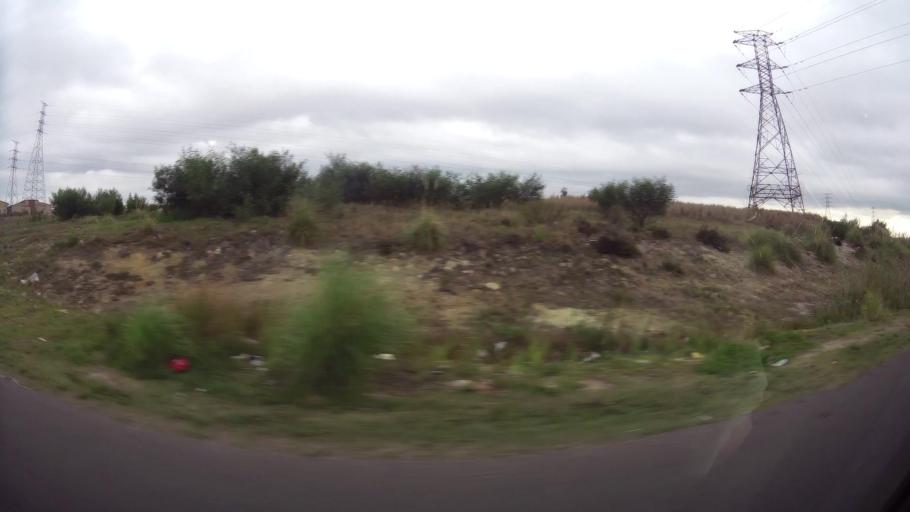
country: ZA
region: Eastern Cape
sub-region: Nelson Mandela Bay Metropolitan Municipality
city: Port Elizabeth
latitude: -33.9209
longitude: 25.5685
